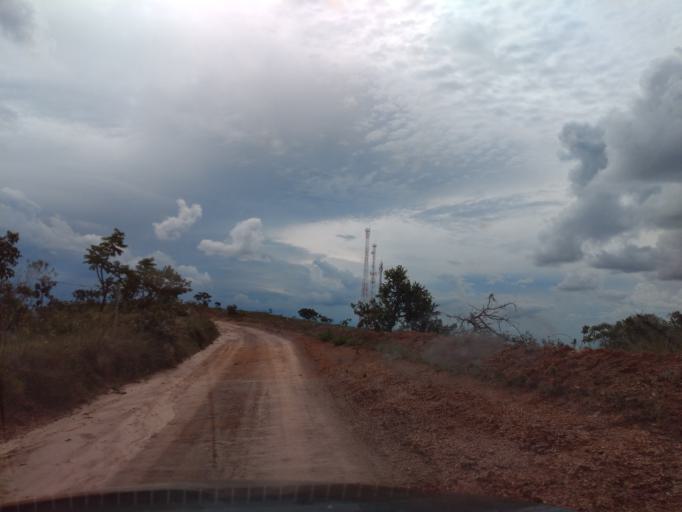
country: BR
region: Minas Gerais
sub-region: Lavras
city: Lavras
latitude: -21.5279
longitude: -44.9003
